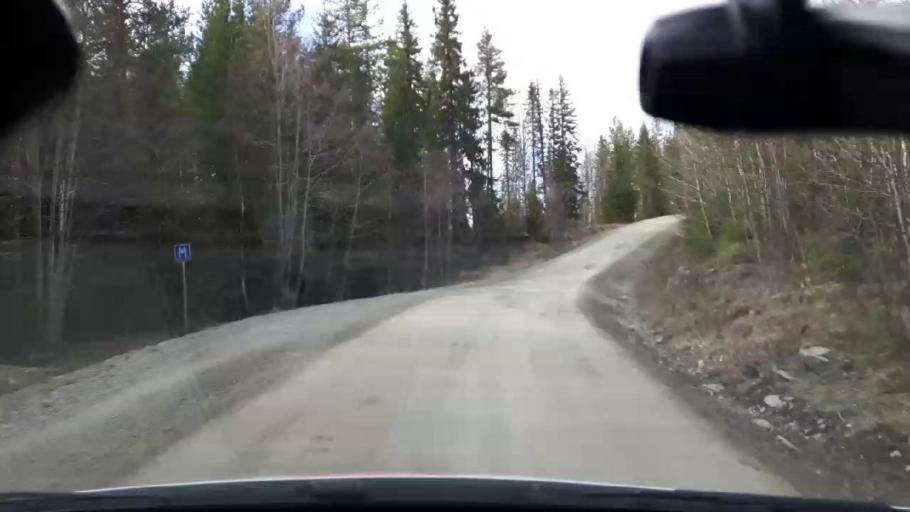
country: SE
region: Jaemtland
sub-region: Bergs Kommun
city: Hoverberg
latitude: 62.9078
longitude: 14.6342
